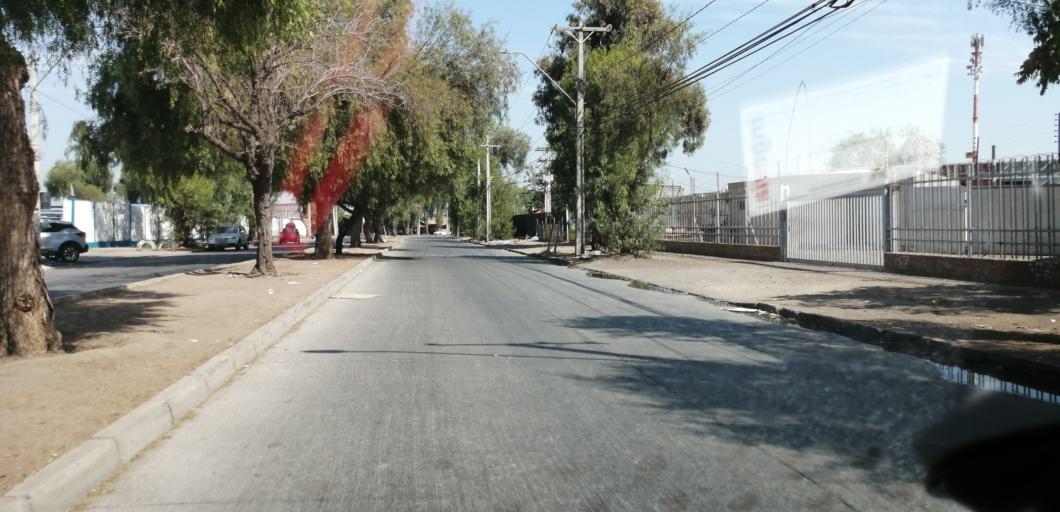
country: CL
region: Santiago Metropolitan
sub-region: Provincia de Santiago
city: Lo Prado
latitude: -33.4563
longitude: -70.7426
